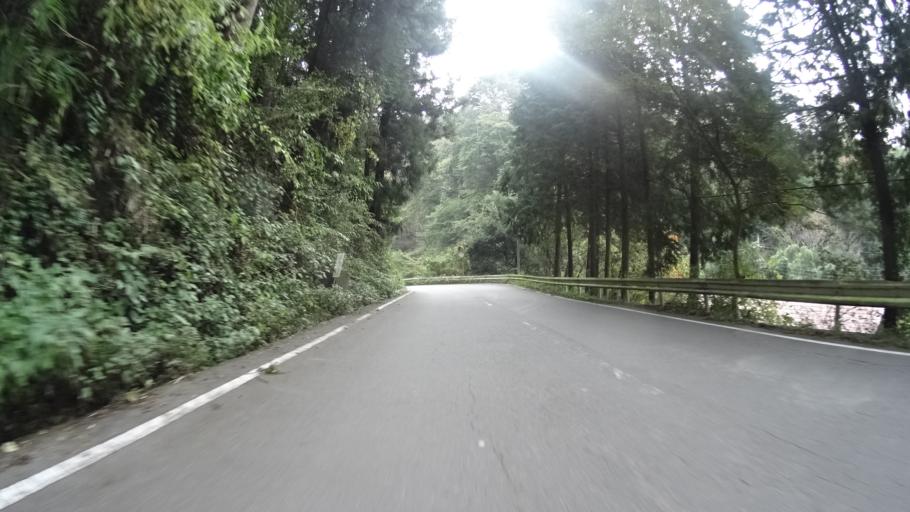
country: JP
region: Yamanashi
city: Uenohara
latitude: 35.6754
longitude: 139.0927
